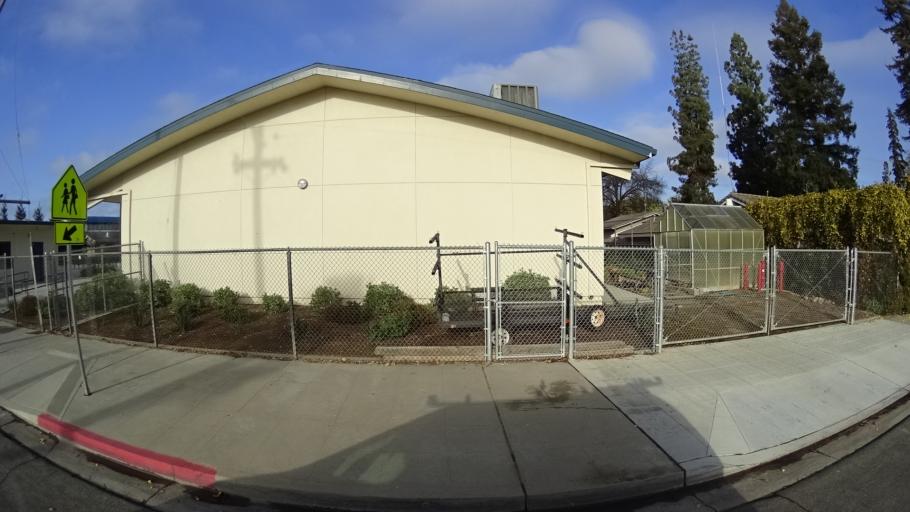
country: US
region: California
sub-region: Fresno County
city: Fresno
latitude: 36.8183
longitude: -119.7972
